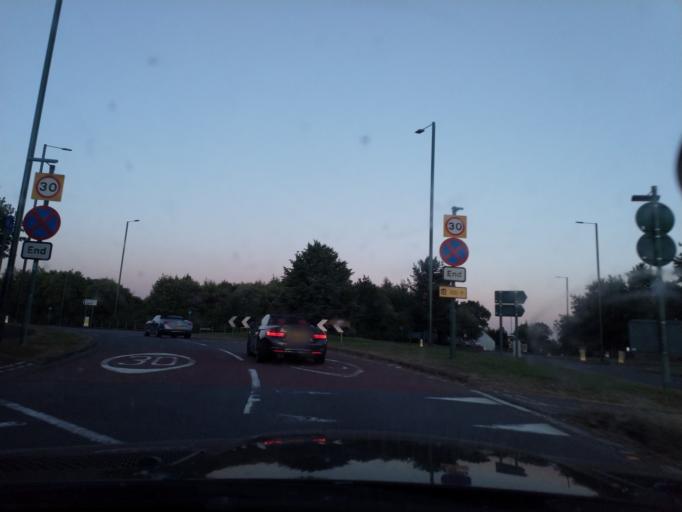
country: GB
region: England
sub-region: Solihull
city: Balsall Common
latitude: 52.4006
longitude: -1.6561
